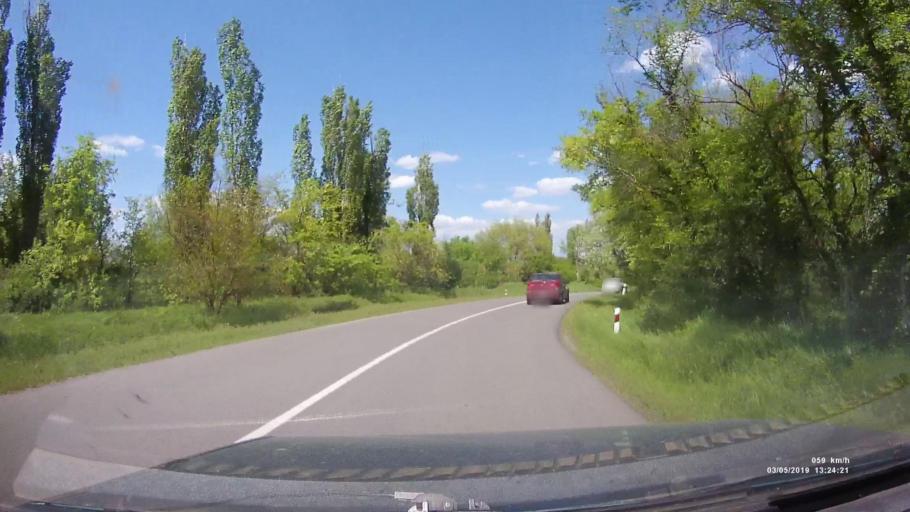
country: RU
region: Rostov
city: Semikarakorsk
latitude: 47.5645
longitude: 40.7955
